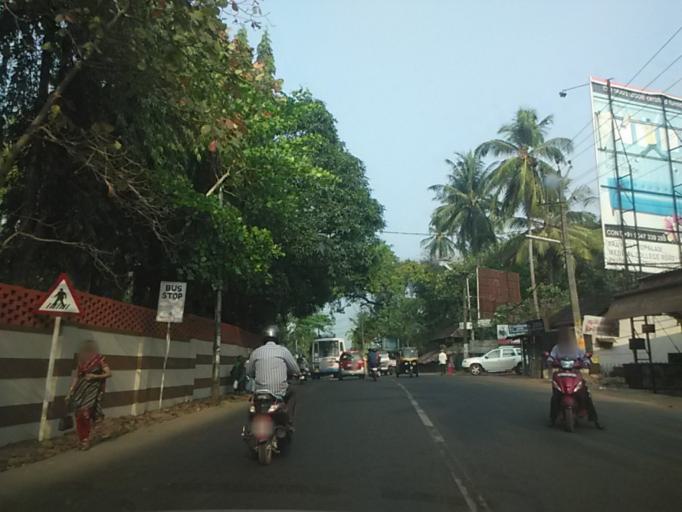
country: IN
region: Kerala
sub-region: Kozhikode
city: Kozhikode
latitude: 11.2871
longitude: 75.8034
